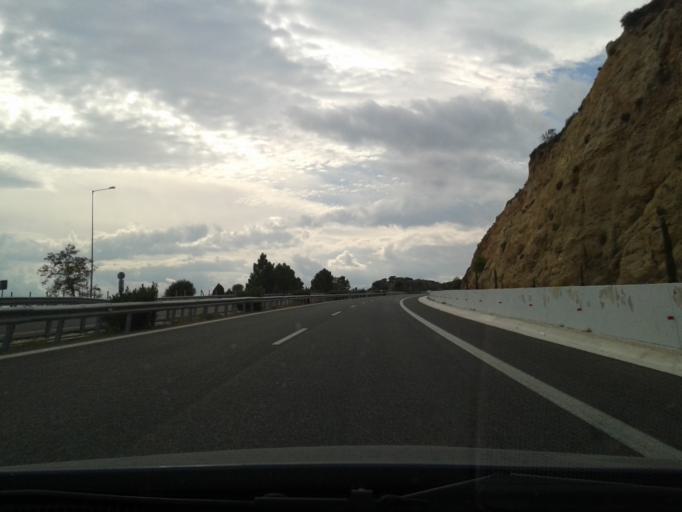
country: GR
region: Peloponnese
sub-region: Nomos Korinthias
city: Nemea
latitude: 37.7878
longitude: 22.7107
